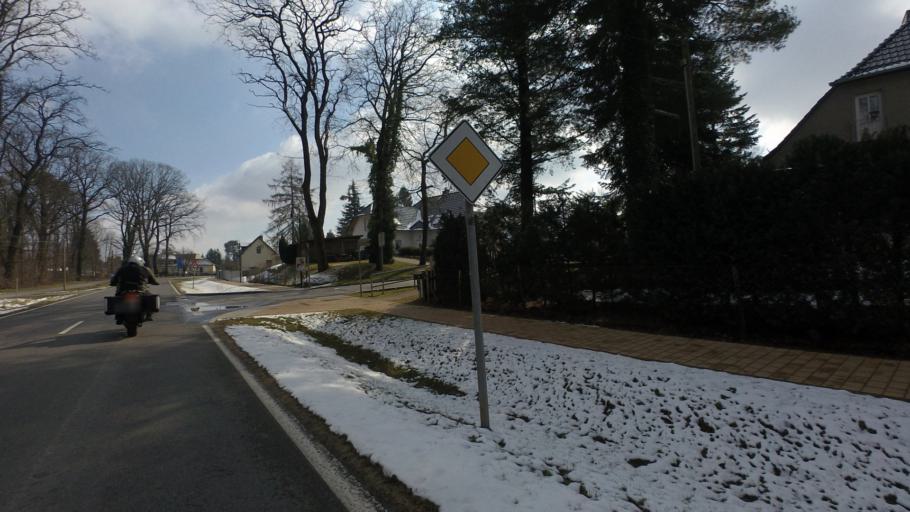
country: DE
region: Berlin
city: Buch
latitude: 52.6805
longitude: 13.5299
